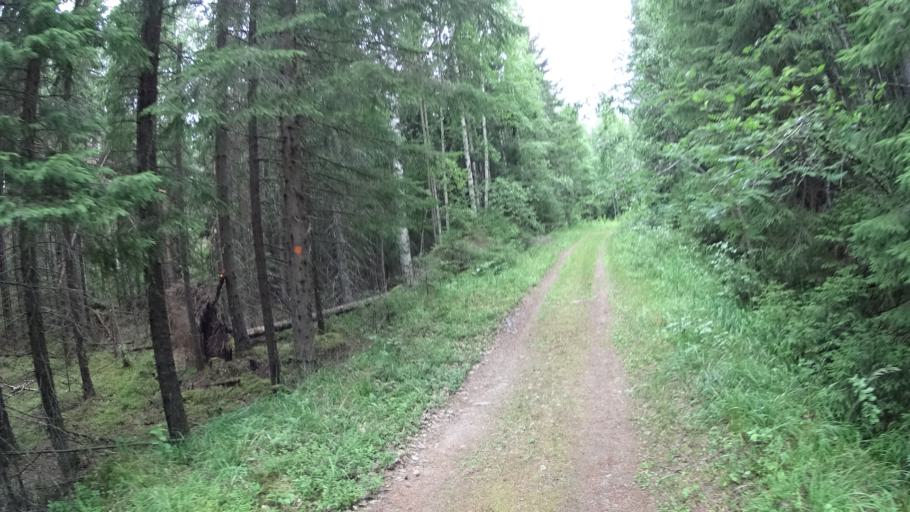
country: FI
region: Southern Savonia
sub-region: Mikkeli
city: Maentyharju
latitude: 61.1870
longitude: 26.8273
